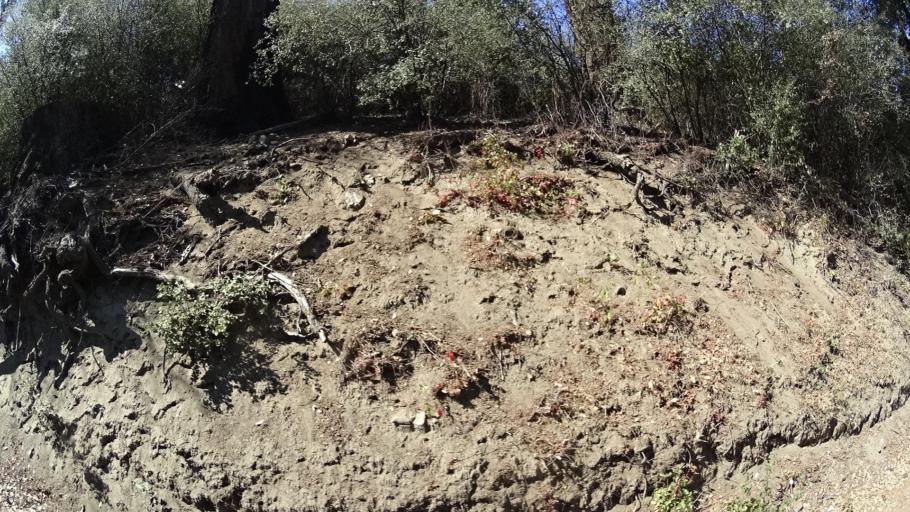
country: US
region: California
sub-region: Riverside County
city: Aguanga
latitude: 33.3404
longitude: -116.9210
